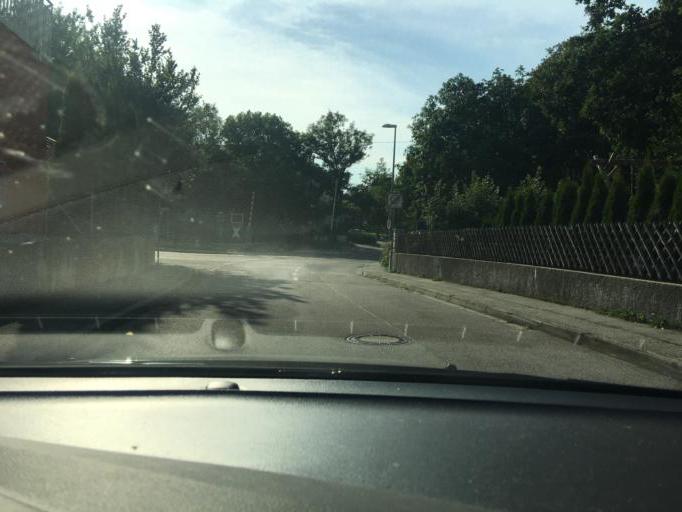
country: DE
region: Bavaria
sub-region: Upper Bavaria
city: Erding
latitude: 48.2959
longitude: 11.9041
